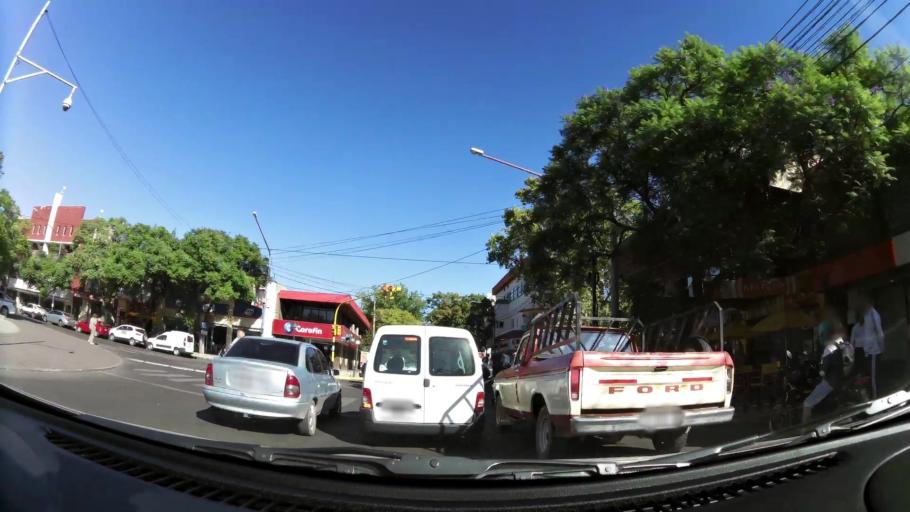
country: AR
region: Mendoza
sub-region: Departamento de Godoy Cruz
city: Godoy Cruz
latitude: -32.9246
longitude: -68.8446
